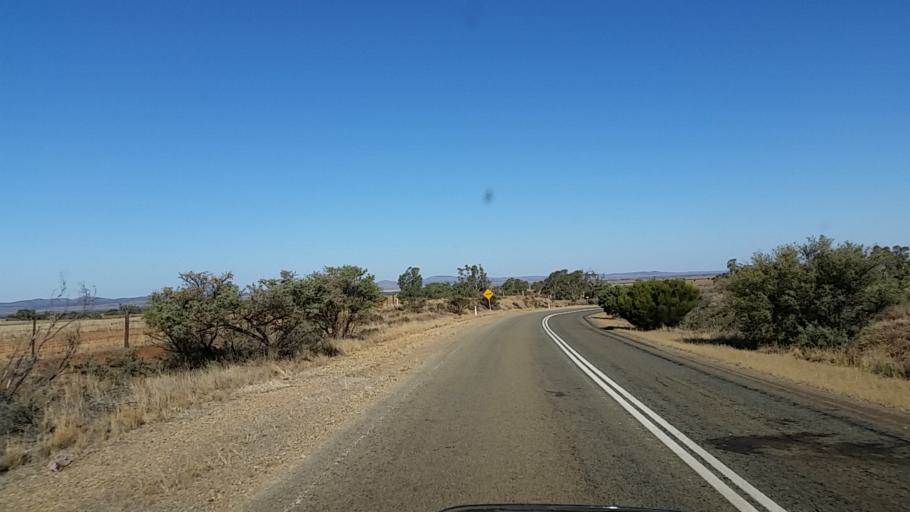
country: AU
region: South Australia
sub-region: Peterborough
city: Peterborough
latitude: -32.6355
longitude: 138.5967
